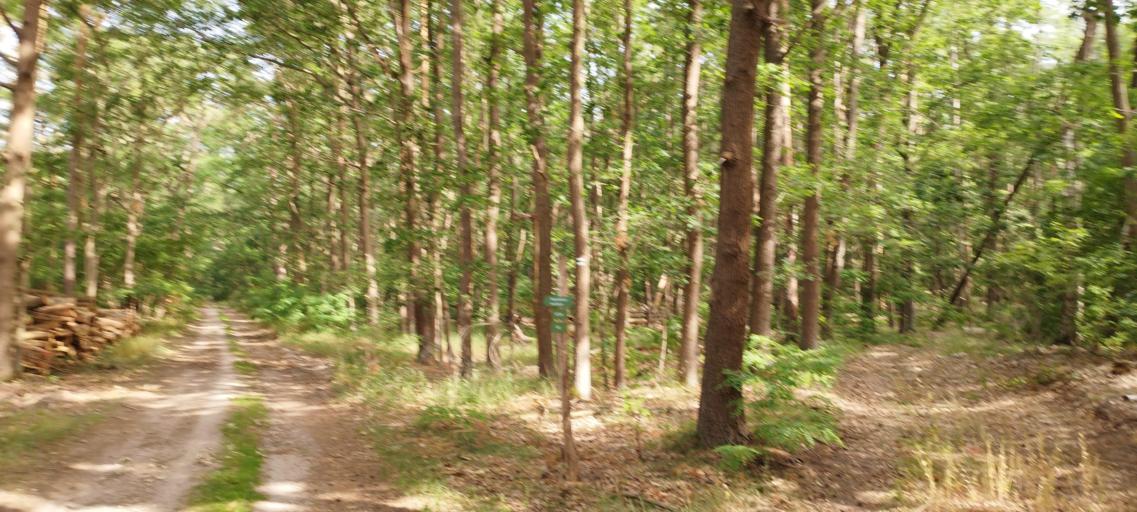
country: DE
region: Brandenburg
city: Bad Saarow
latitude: 52.2979
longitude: 14.0390
